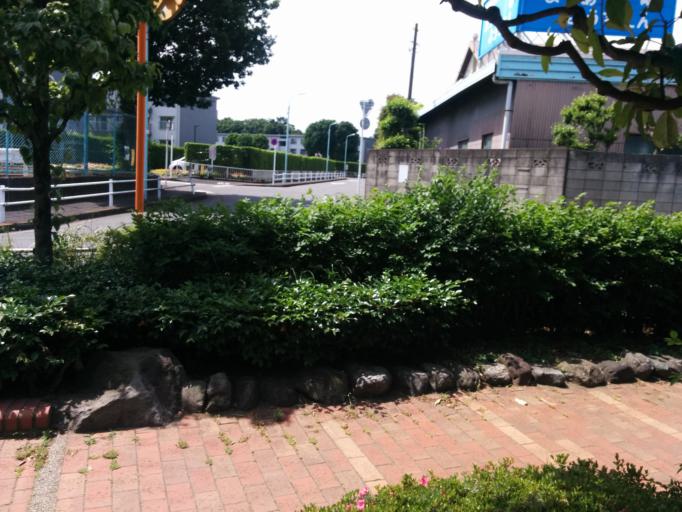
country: JP
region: Tokyo
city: Higashimurayama-shi
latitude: 35.7661
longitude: 139.4877
